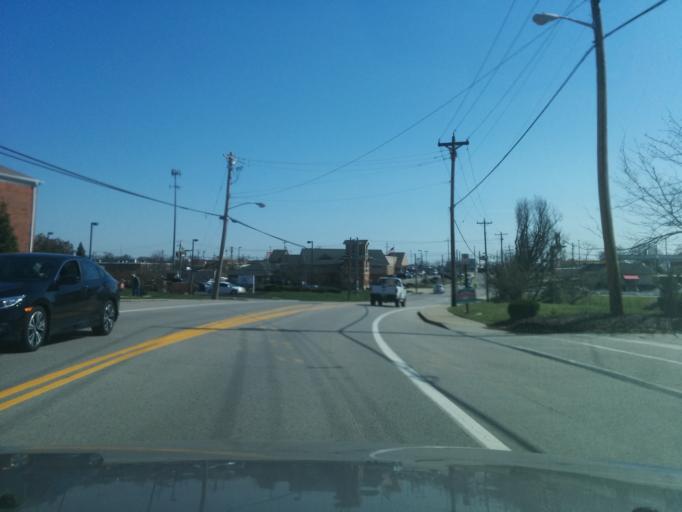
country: US
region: Ohio
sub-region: Hamilton County
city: Monfort Heights
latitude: 39.1892
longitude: -84.6048
